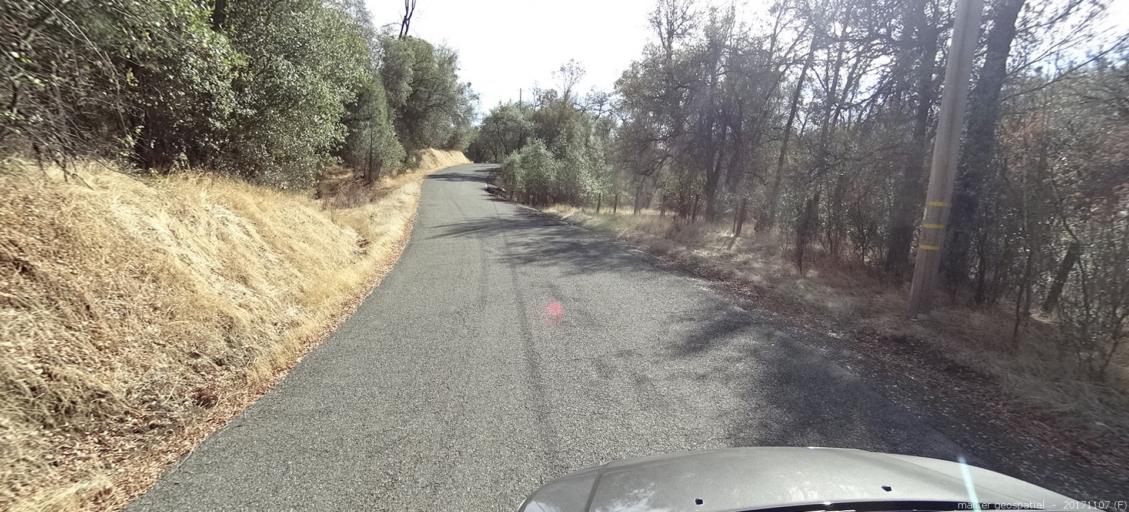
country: US
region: California
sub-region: Shasta County
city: Shasta
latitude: 40.5238
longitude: -122.5548
